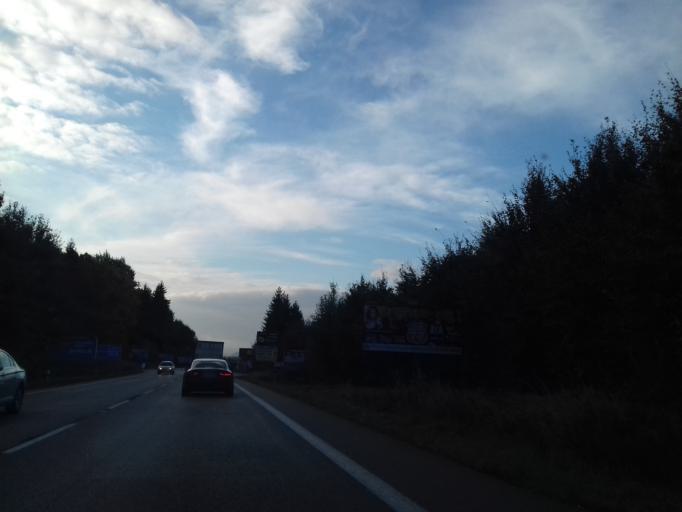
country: SK
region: Zilinsky
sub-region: Okres Zilina
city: Zilina
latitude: 49.2021
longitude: 18.7947
